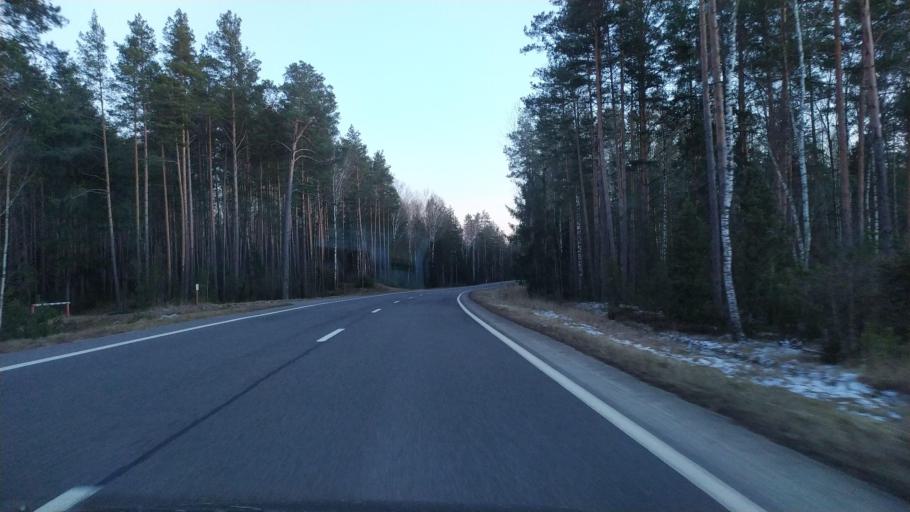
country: BY
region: Brest
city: Pruzhany
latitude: 52.5202
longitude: 24.1773
